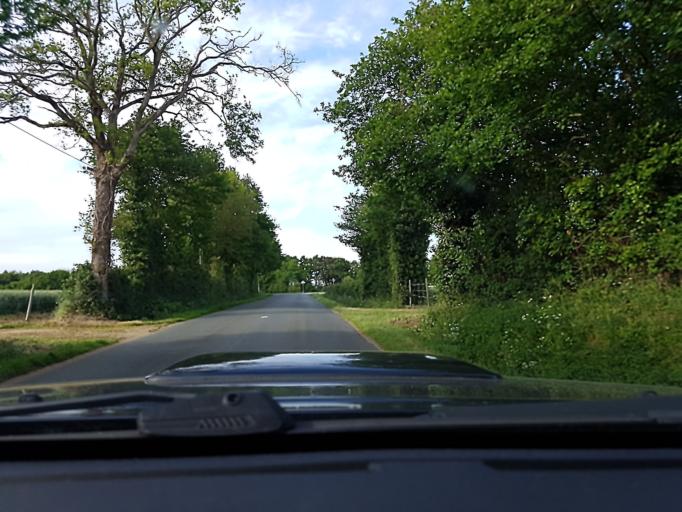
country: FR
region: Pays de la Loire
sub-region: Departement de la Vendee
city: Mache
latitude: 46.7505
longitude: -1.6741
